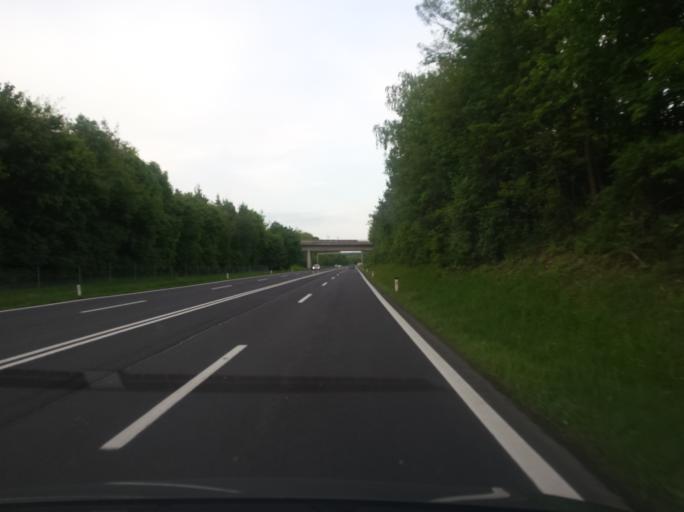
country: AT
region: Burgenland
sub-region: Politischer Bezirk Mattersburg
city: Mattersburg
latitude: 47.7440
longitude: 16.3797
